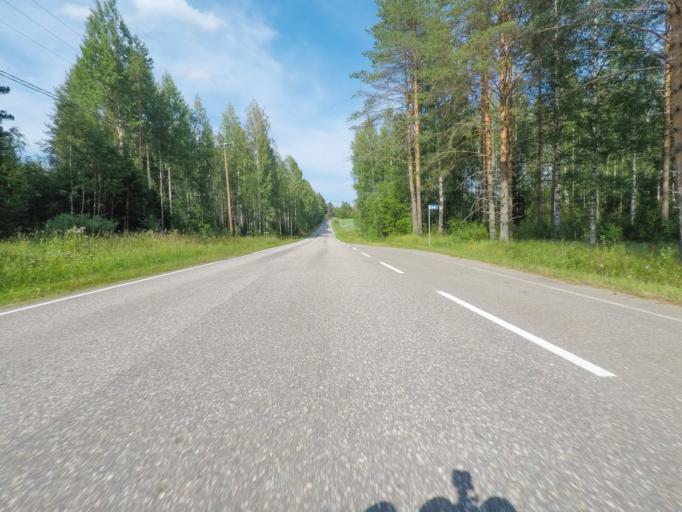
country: FI
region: Southern Savonia
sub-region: Savonlinna
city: Sulkava
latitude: 61.7593
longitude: 28.2296
